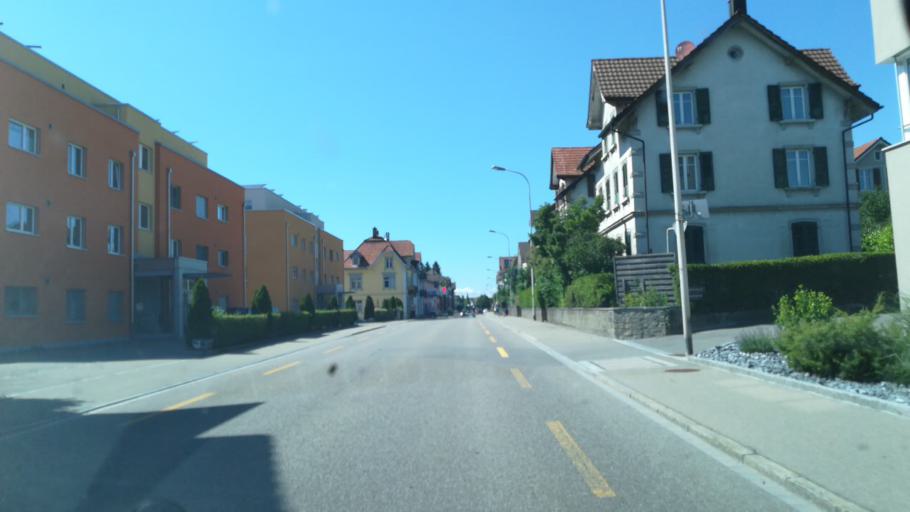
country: CH
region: Saint Gallen
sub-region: Wahlkreis St. Gallen
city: Gossau
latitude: 47.4177
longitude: 9.2442
